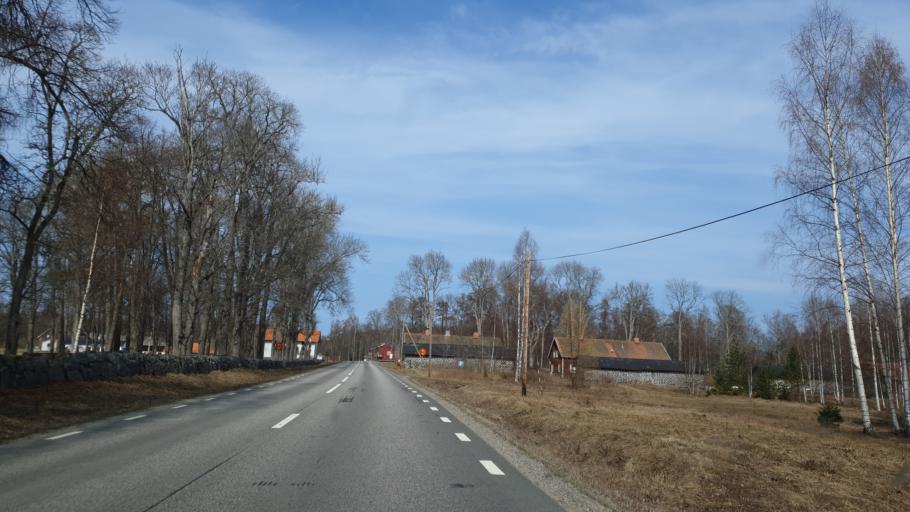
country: SE
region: Gaevleborg
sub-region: Gavle Kommun
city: Norrsundet
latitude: 61.0450
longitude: 17.1447
